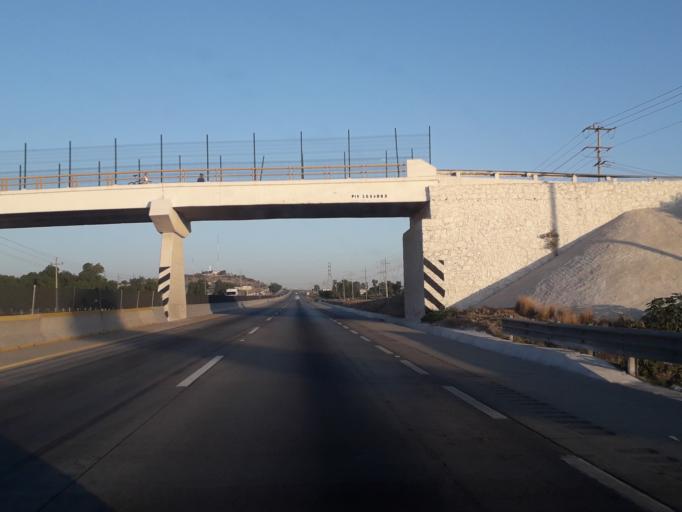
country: MX
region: Puebla
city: Acatzingo de Hidalgo
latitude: 18.9694
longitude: -97.7884
